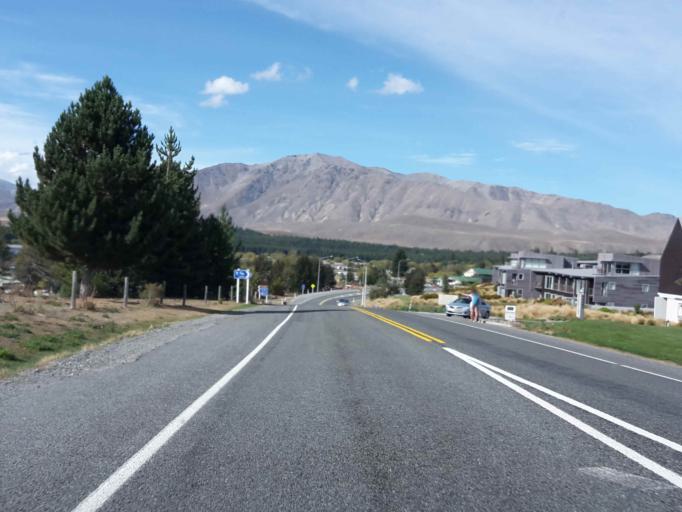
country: NZ
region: Canterbury
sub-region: Timaru District
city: Pleasant Point
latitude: -44.0029
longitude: 170.4719
